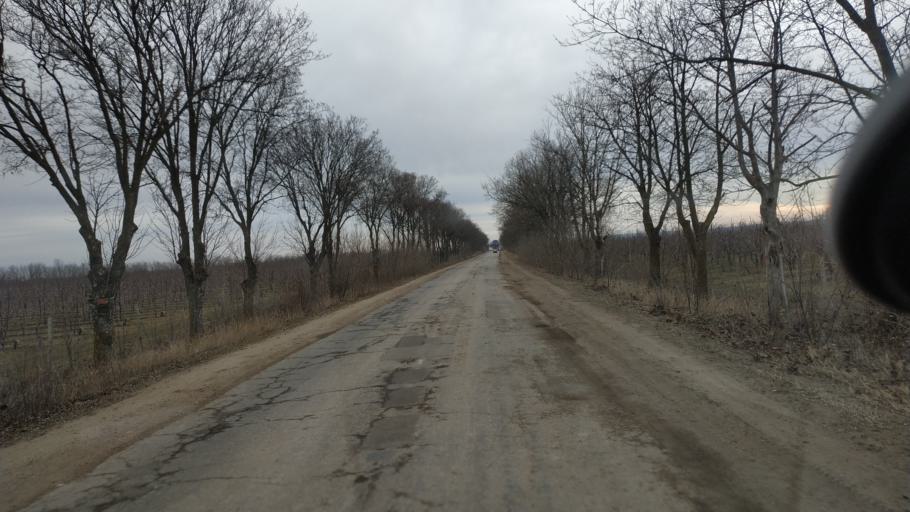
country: MD
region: Telenesti
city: Cocieri
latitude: 47.2658
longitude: 29.1025
